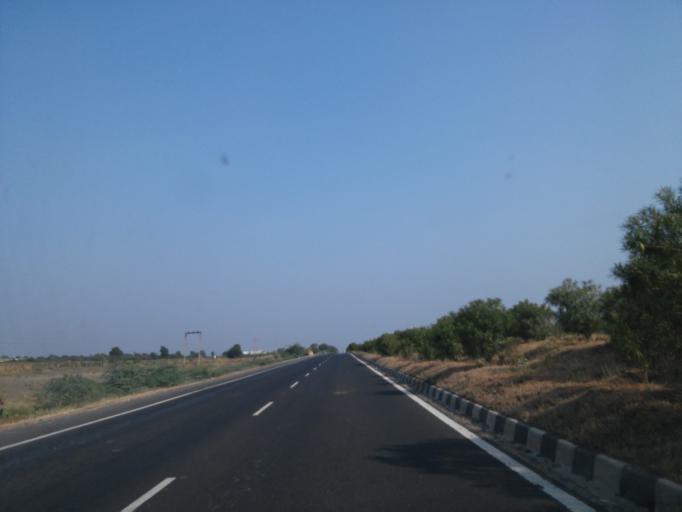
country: IN
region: Gujarat
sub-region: Surendranagar
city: Halvad
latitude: 23.0052
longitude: 71.1072
